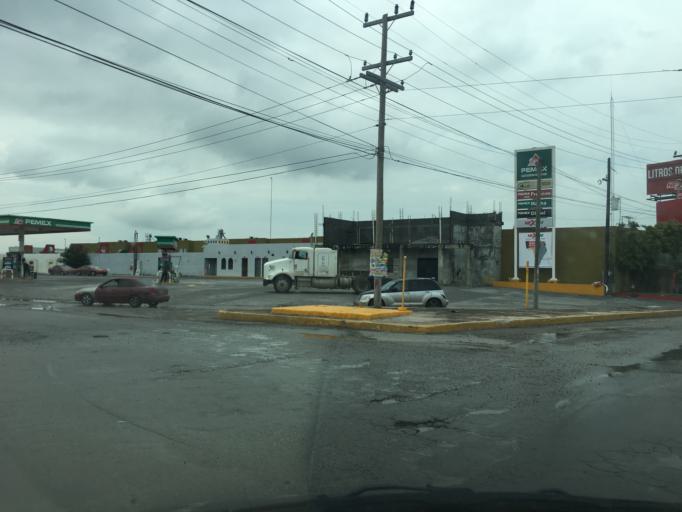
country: MX
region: Tamaulipas
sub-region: Matamoros
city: Heroica Matamoros
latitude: 25.8778
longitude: -97.5272
